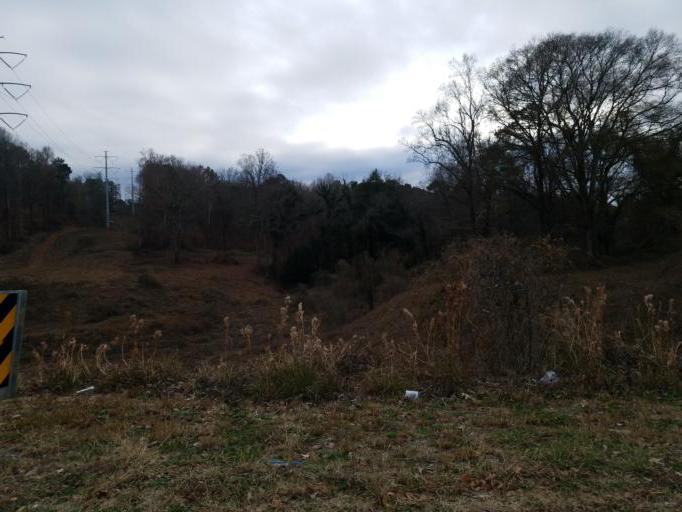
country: US
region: Georgia
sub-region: Cherokee County
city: Canton
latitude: 34.2234
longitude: -84.5010
